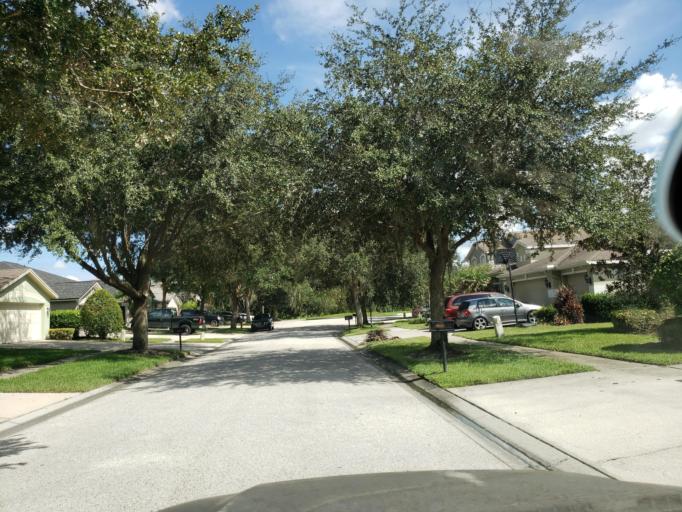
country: US
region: Florida
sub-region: Hillsborough County
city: Fish Hawk
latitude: 27.8332
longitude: -82.2140
